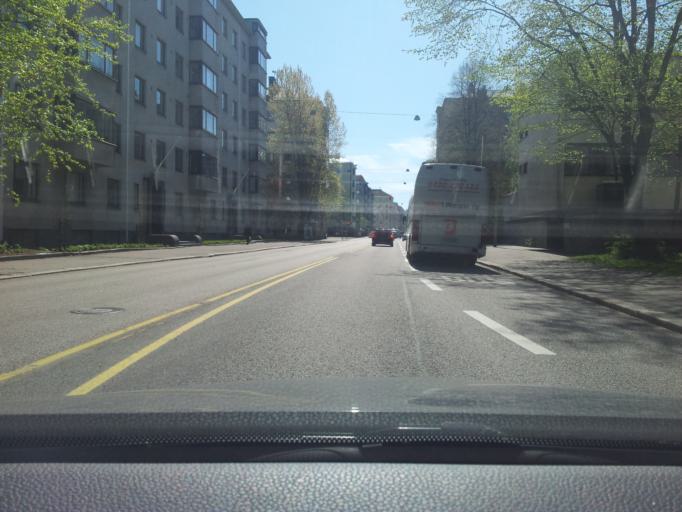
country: FI
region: Uusimaa
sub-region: Helsinki
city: Helsinki
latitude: 60.1864
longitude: 24.9153
